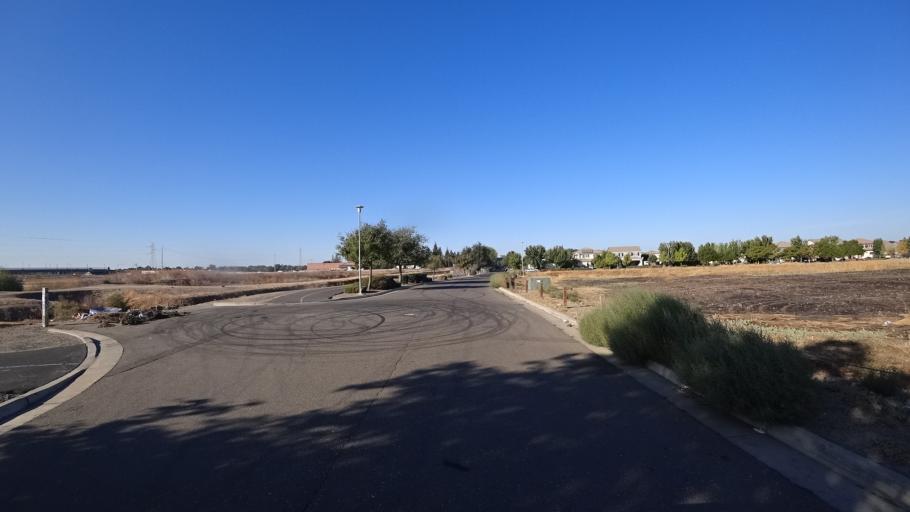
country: US
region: California
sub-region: Sacramento County
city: Parkway
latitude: 38.4712
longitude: -121.4953
